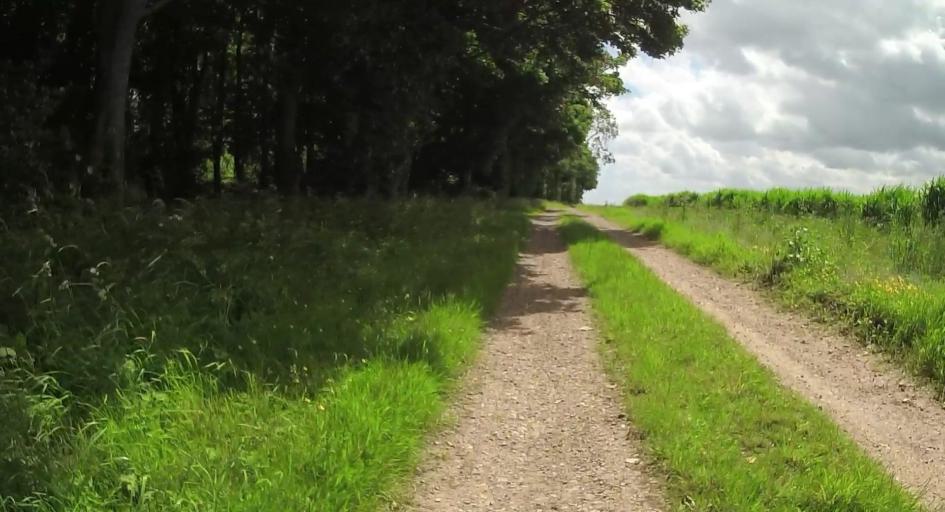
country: GB
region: England
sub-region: Hampshire
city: Basingstoke
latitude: 51.1809
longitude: -1.1645
